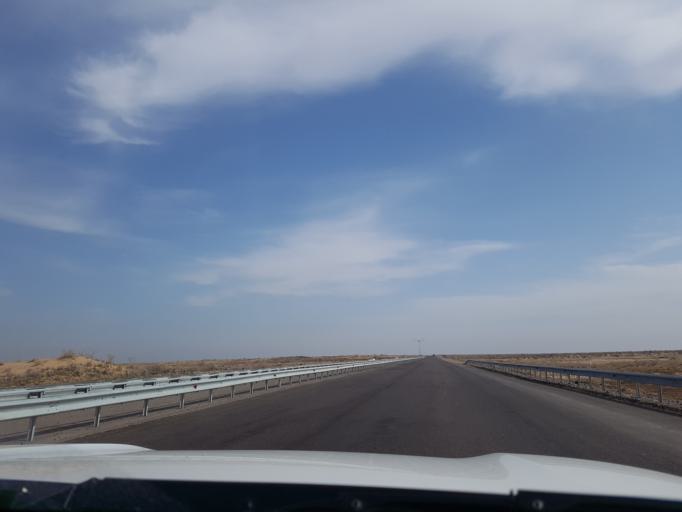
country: TM
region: Mary
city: Mary
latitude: 37.2751
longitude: 61.3055
